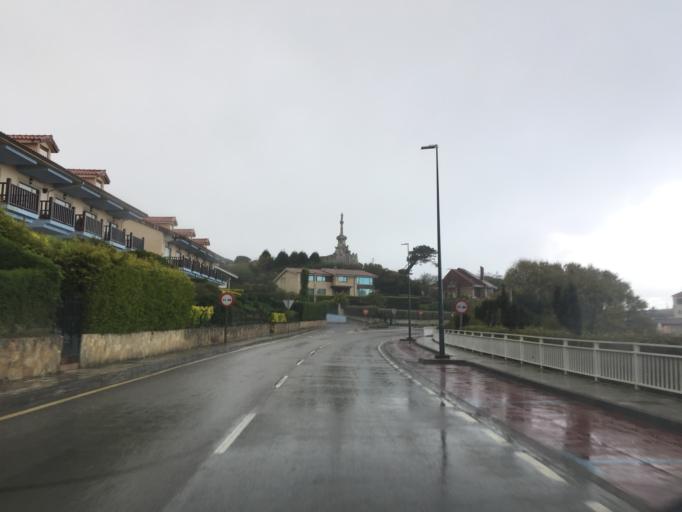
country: ES
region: Cantabria
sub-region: Provincia de Cantabria
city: Comillas
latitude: 43.3886
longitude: -4.2887
